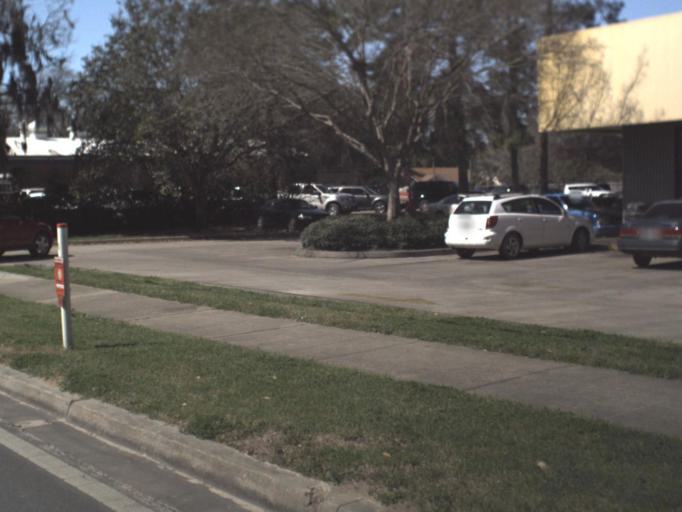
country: US
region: Florida
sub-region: Gadsden County
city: Quincy
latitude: 30.5856
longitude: -84.6004
